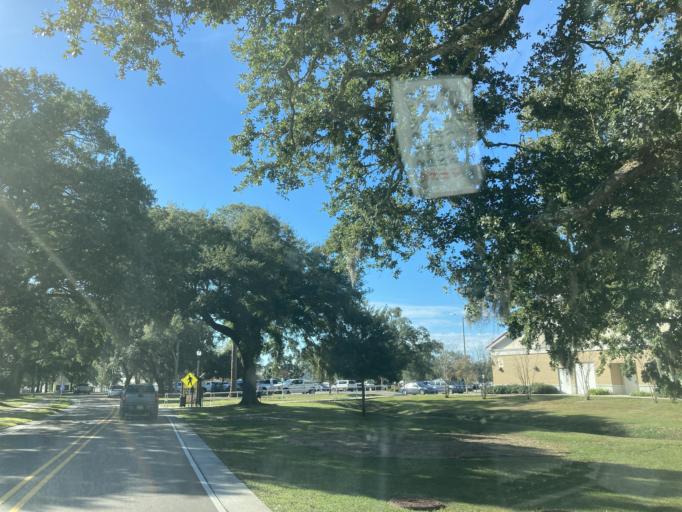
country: US
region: Mississippi
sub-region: Harrison County
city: D'Iberville
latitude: 30.4112
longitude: -88.9468
